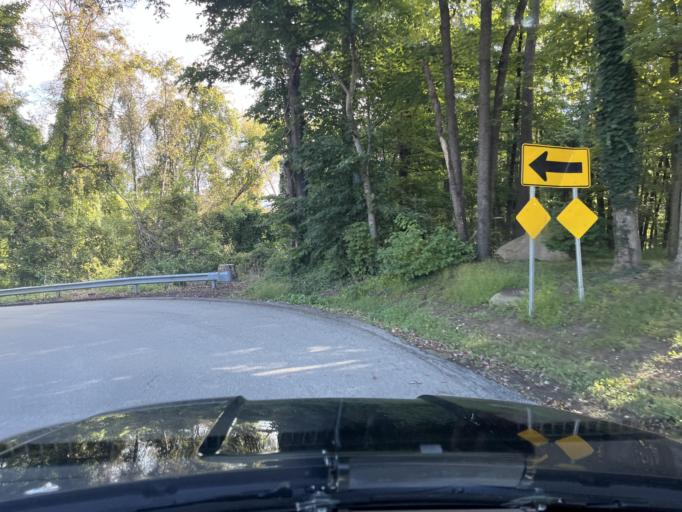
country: US
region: Pennsylvania
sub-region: Fayette County
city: South Uniontown
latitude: 39.8896
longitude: -79.7563
